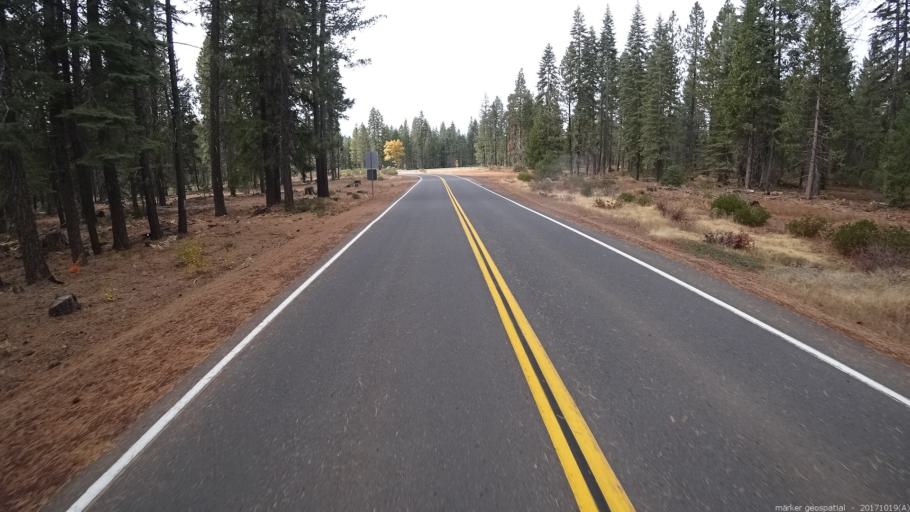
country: US
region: California
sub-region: Shasta County
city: Burney
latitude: 41.1454
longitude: -121.6455
